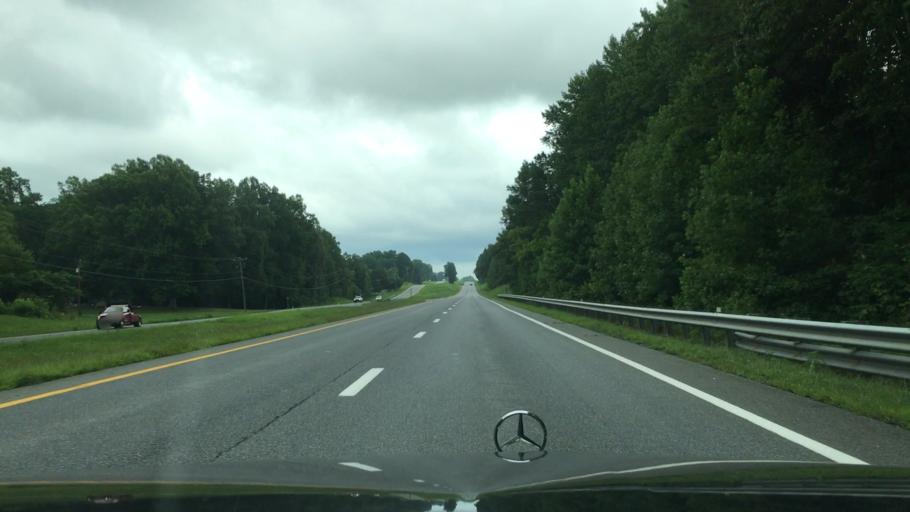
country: US
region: Virginia
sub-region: Appomattox County
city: Appomattox
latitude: 37.2829
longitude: -78.7108
